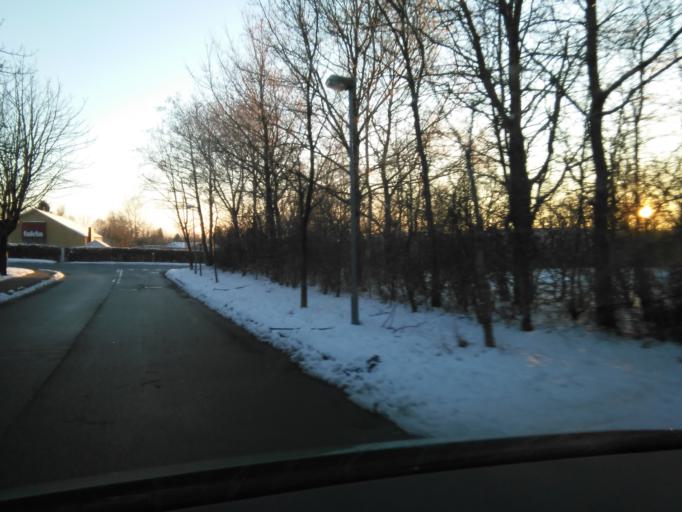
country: DK
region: Central Jutland
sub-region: Arhus Kommune
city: Kolt
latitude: 56.1099
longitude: 10.0781
